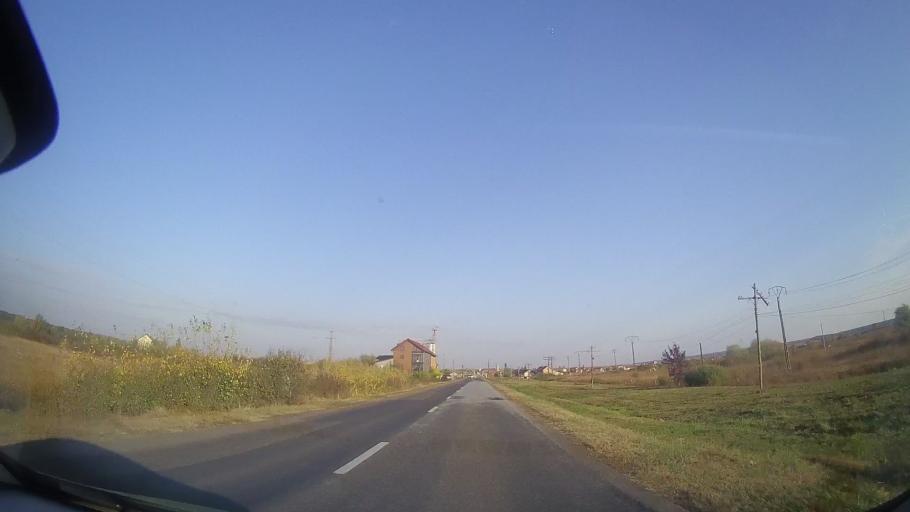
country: RO
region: Timis
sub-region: Comuna Pischia
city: Pischia
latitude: 45.8941
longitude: 21.3455
